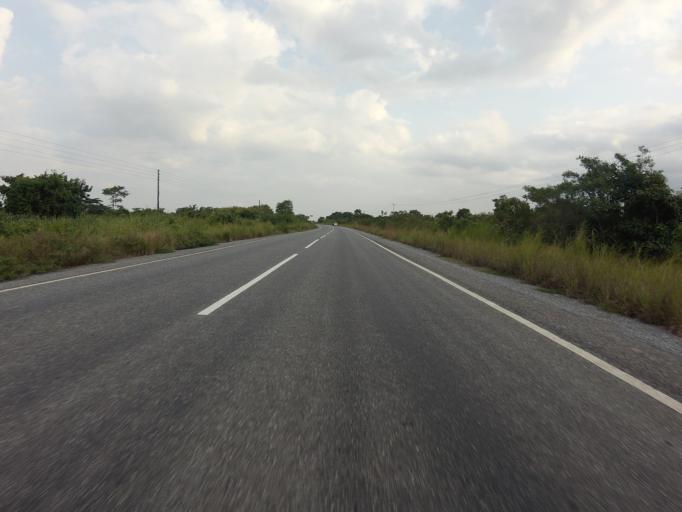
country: GH
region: Volta
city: Ho
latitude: 6.3555
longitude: 0.5369
